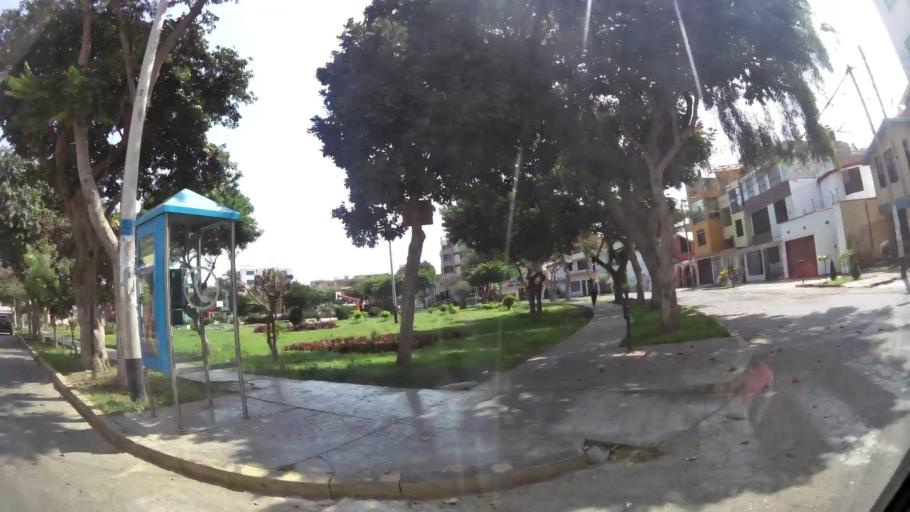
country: PE
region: La Libertad
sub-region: Provincia de Trujillo
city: Trujillo
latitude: -8.1255
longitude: -79.0381
